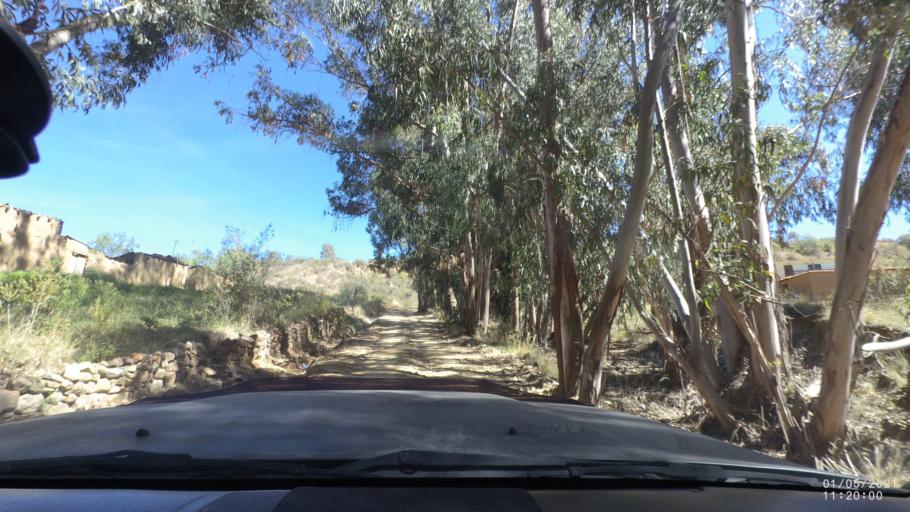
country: BO
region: Cochabamba
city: Tarata
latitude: -17.6440
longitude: -66.1227
